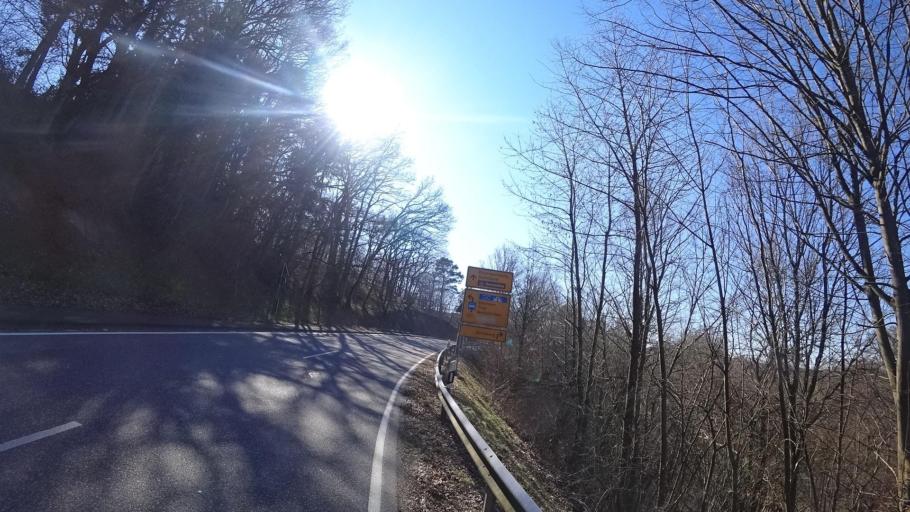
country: DE
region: Rheinland-Pfalz
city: Unzenberg
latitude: 49.9605
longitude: 7.4567
